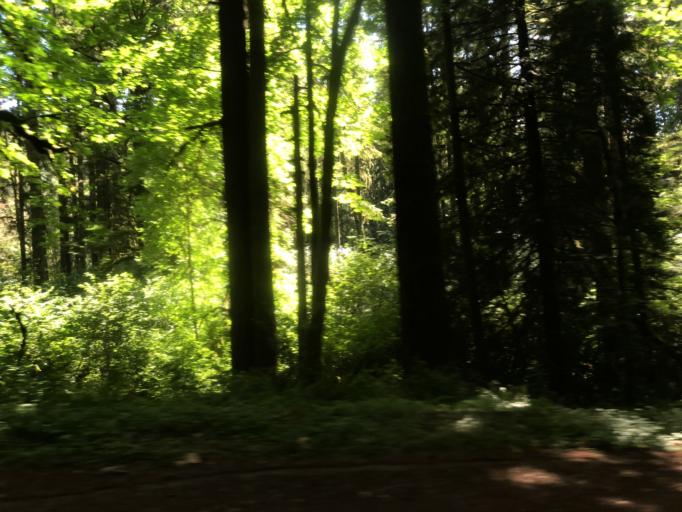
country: US
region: Oregon
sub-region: Clackamas County
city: Sandy
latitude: 45.4260
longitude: -122.2250
